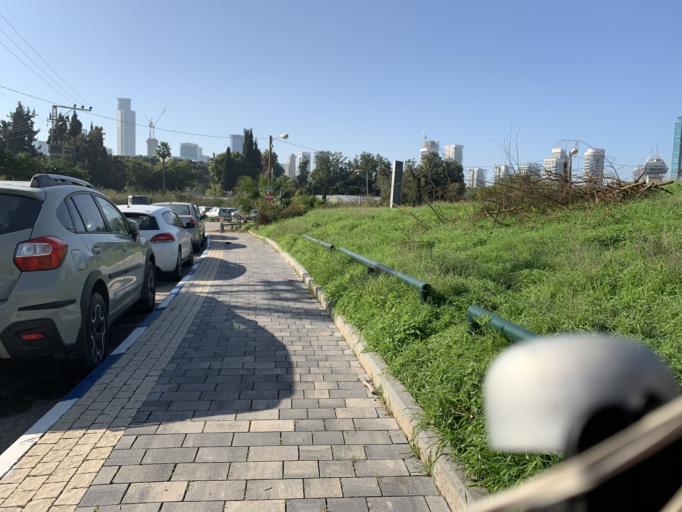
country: IL
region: Tel Aviv
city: Ramat Gan
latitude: 32.0947
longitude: 34.8091
